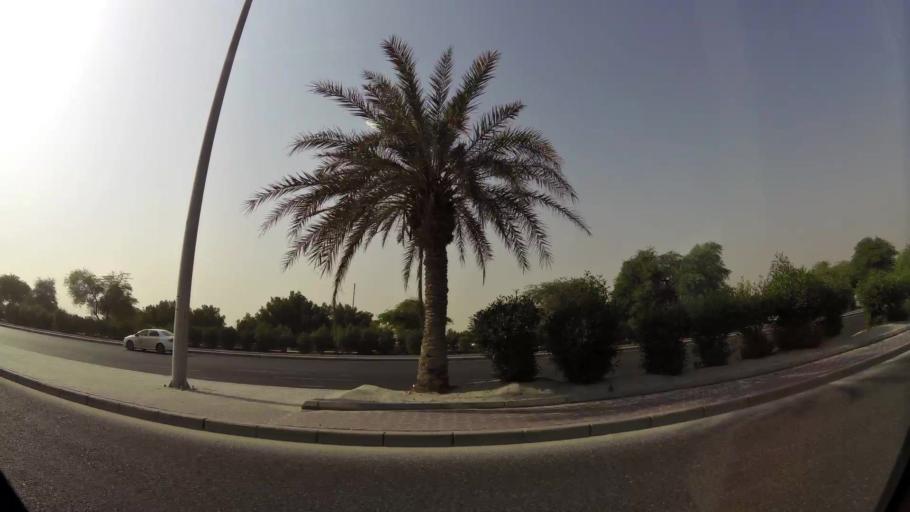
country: KW
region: Al Asimah
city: Ar Rabiyah
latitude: 29.2806
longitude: 47.8368
